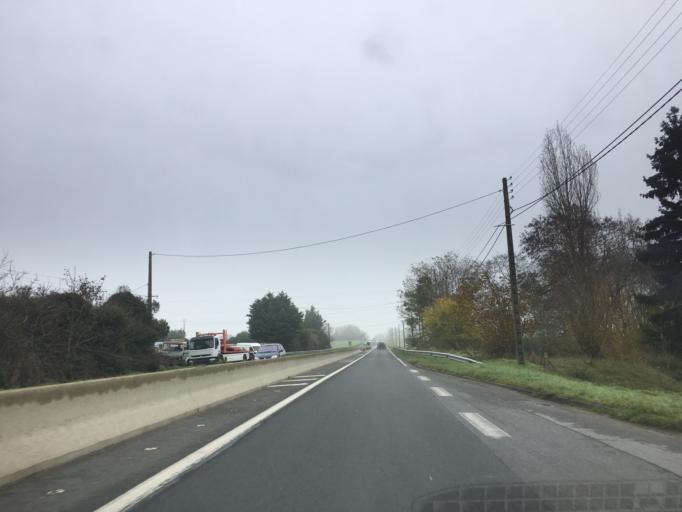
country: FR
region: Ile-de-France
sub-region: Departement de Seine-et-Marne
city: Vernou-la-Celle-sur-Seine
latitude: 48.3641
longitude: 2.8543
